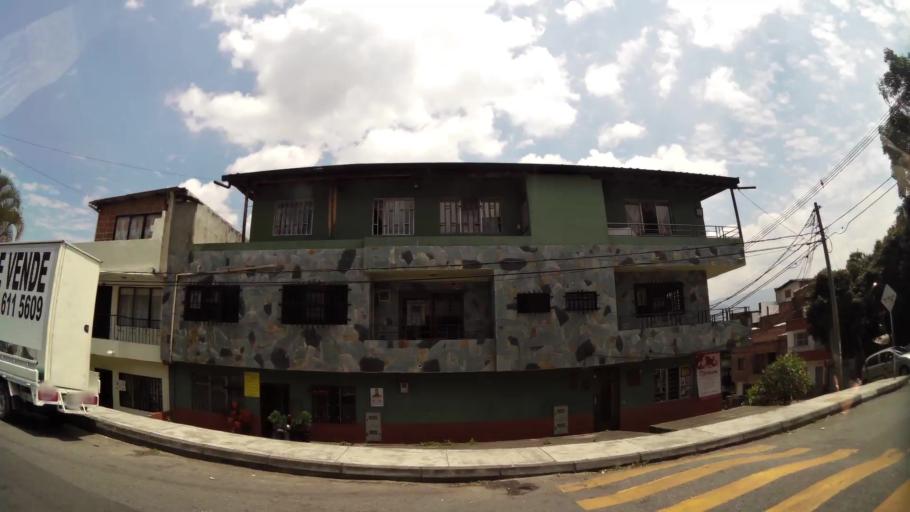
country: CO
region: Antioquia
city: Bello
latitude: 6.3080
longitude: -75.5669
